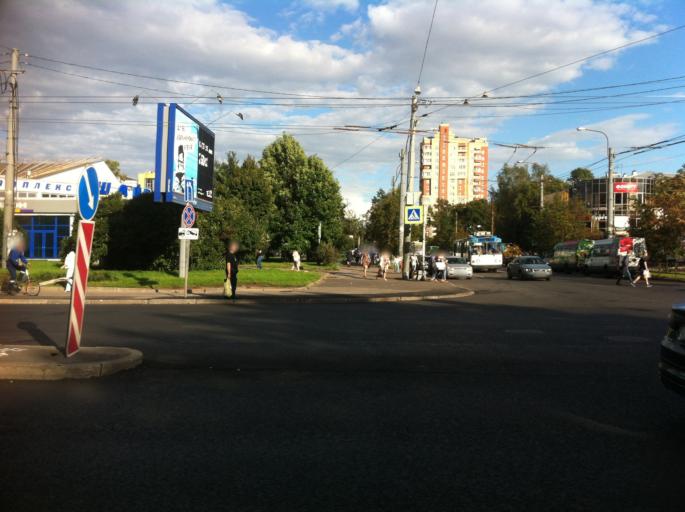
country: RU
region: St.-Petersburg
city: Avtovo
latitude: 59.8804
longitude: 30.2615
